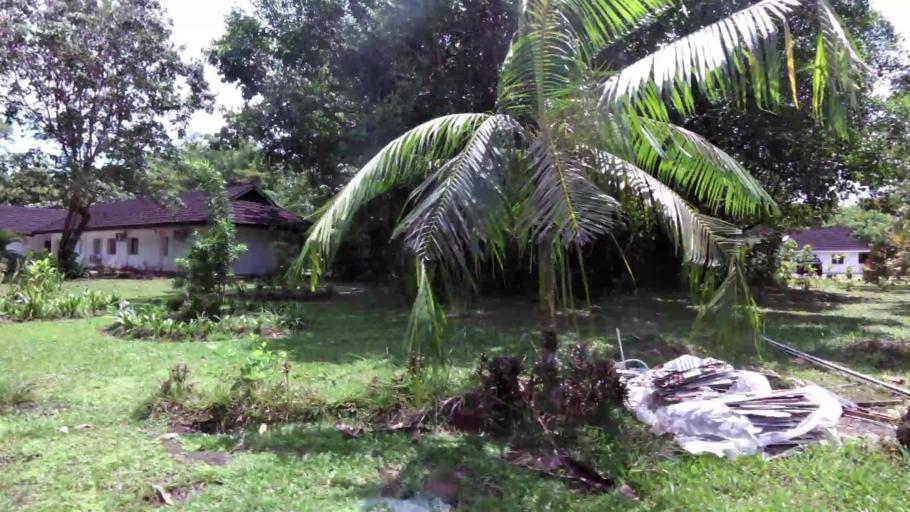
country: BN
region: Belait
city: Kuala Belait
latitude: 4.5954
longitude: 114.2646
